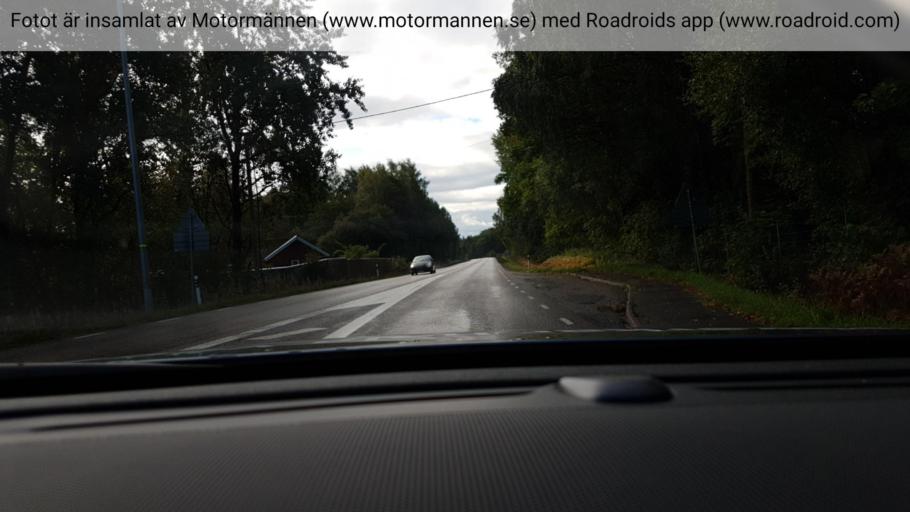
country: SE
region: Vaestra Goetaland
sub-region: Harryda Kommun
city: Ravlanda
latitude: 57.6185
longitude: 12.4347
